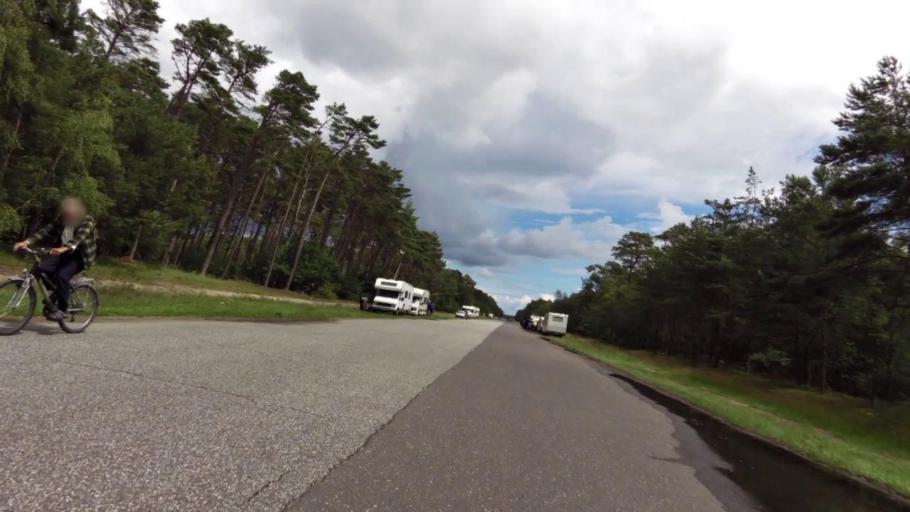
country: PL
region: West Pomeranian Voivodeship
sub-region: Powiat slawienski
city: Darlowo
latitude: 54.5219
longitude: 16.4978
